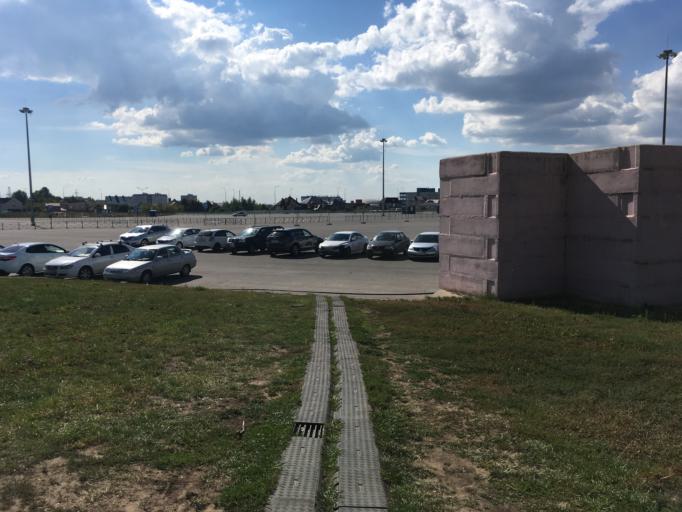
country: RU
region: Samara
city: Samara
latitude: 53.2740
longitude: 50.2363
